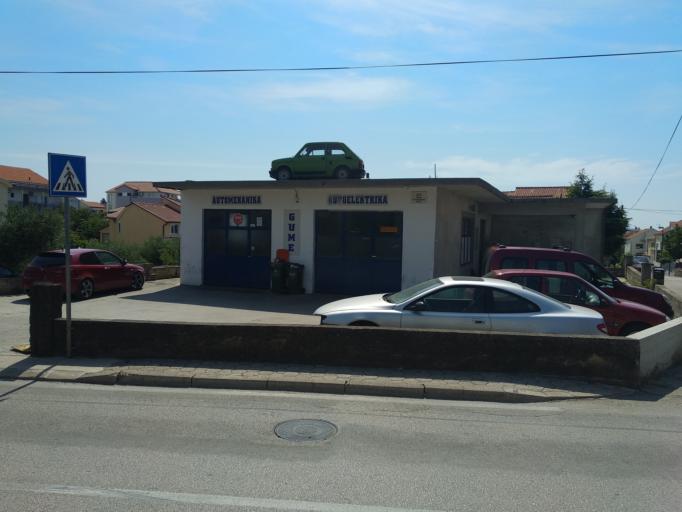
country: HR
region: Sibensko-Kniniska
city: Vodice
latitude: 43.7633
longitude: 15.7731
